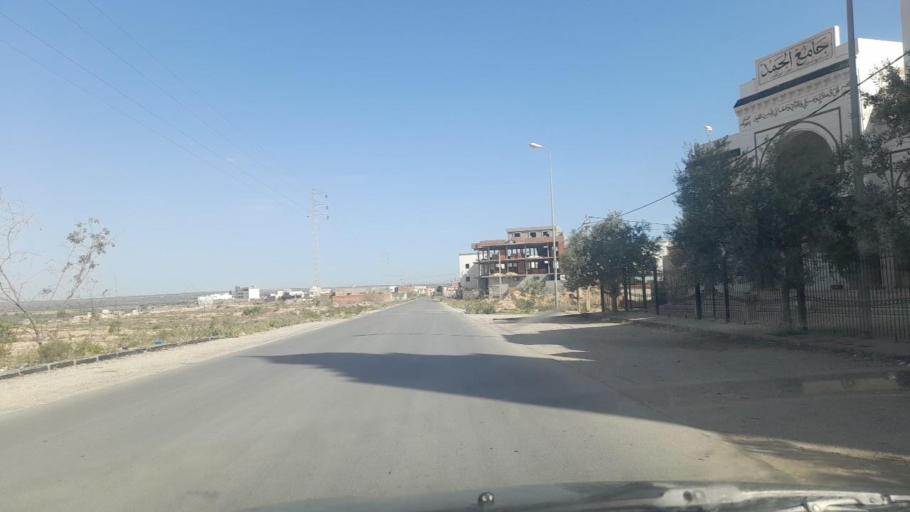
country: TN
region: Susah
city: Akouda
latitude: 35.8131
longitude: 10.5598
